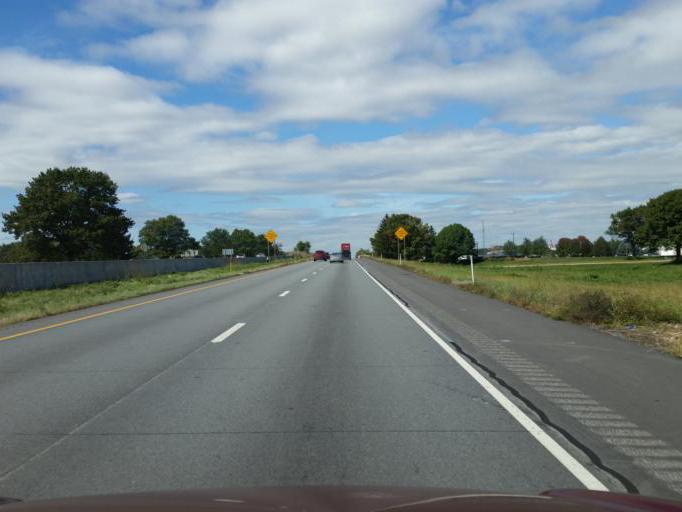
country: US
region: Pennsylvania
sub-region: Lancaster County
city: Salunga
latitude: 40.1113
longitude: -76.4423
